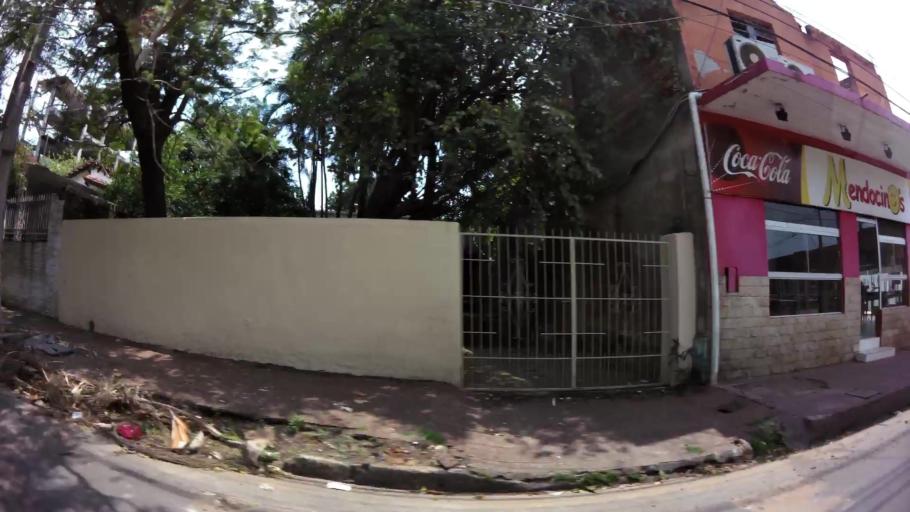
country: PY
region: Central
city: Lambare
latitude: -25.3131
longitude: -57.5714
